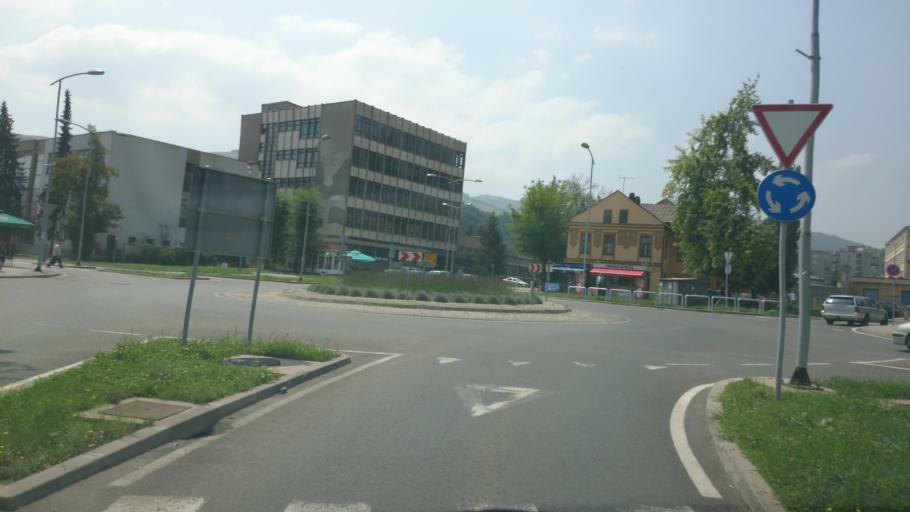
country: BA
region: Federation of Bosnia and Herzegovina
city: Zenica
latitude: 44.2018
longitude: 17.9026
